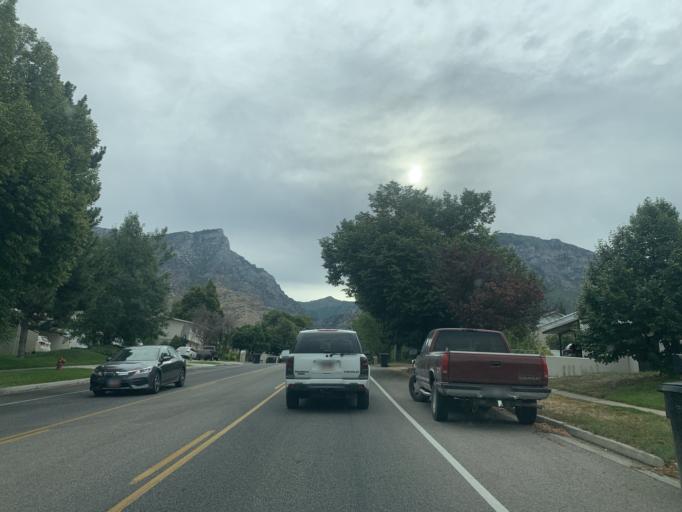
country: US
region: Utah
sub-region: Utah County
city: Provo
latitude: 40.2630
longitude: -111.6519
